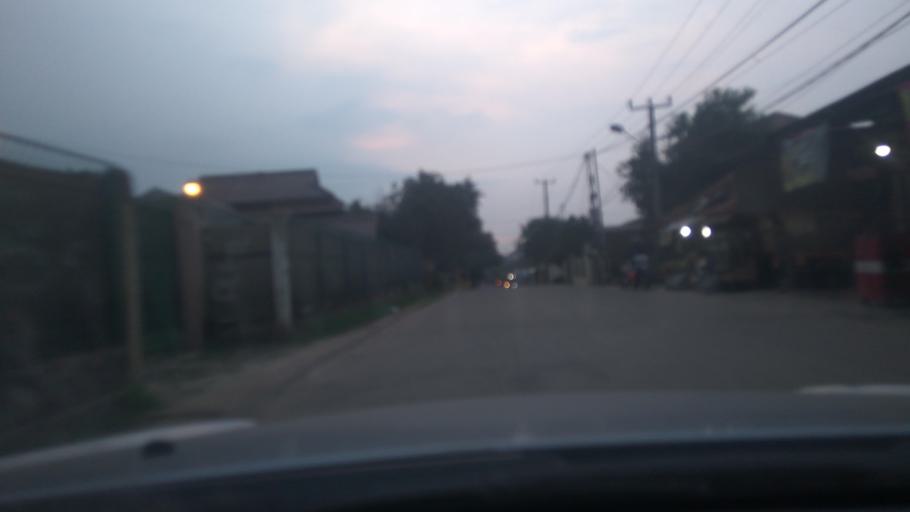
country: ID
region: West Java
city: Pamulang
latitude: -6.3693
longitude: 106.7407
